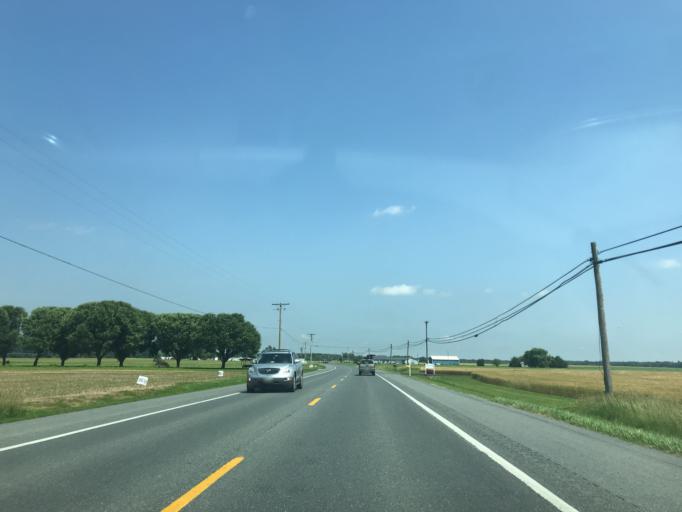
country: US
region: Maryland
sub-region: Dorchester County
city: Hurlock
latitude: 38.5839
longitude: -75.8568
